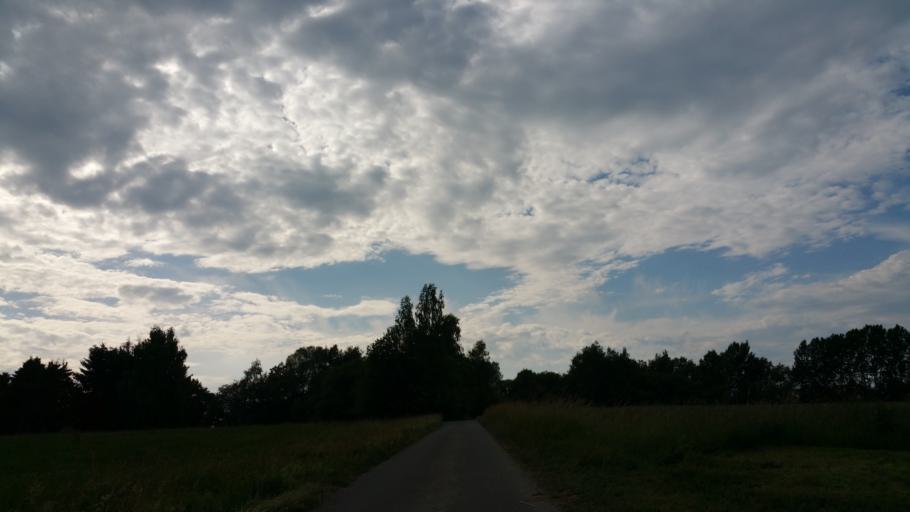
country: DE
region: Bavaria
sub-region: Upper Franconia
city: Schwarzenbach an der Saale
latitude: 50.2119
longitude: 11.9262
